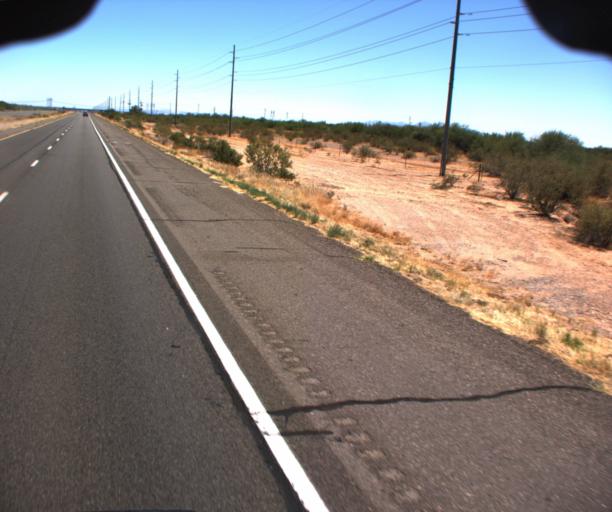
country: US
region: Arizona
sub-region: Maricopa County
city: Sun City West
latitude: 33.7002
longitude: -112.4294
